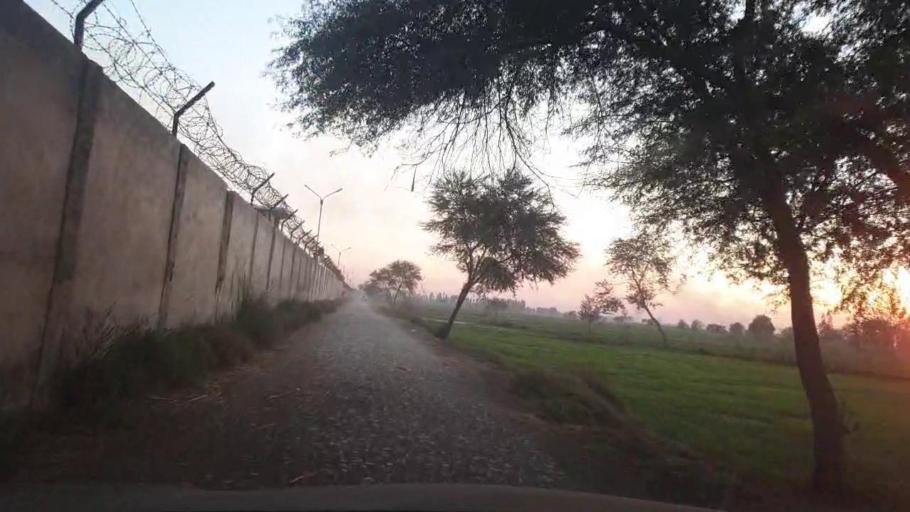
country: PK
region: Sindh
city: Ghotki
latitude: 28.0534
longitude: 69.3604
